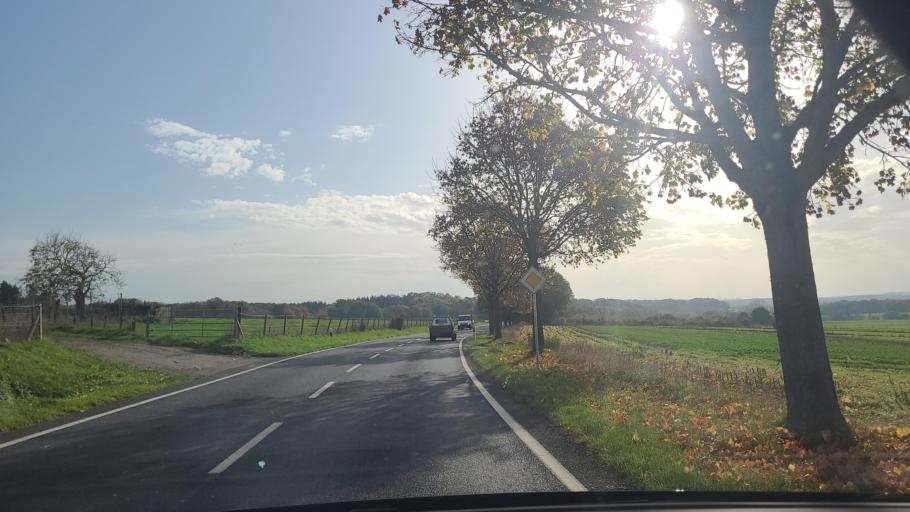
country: LU
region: Luxembourg
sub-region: Canton de Capellen
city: Kehlen
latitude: 49.6617
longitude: 6.0356
